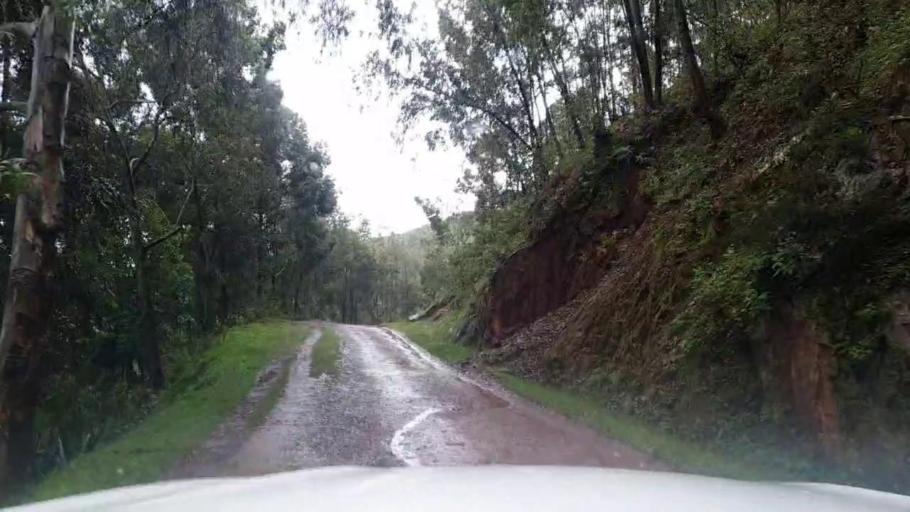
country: RW
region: Kigali
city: Kigali
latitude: -1.7620
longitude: 29.9922
